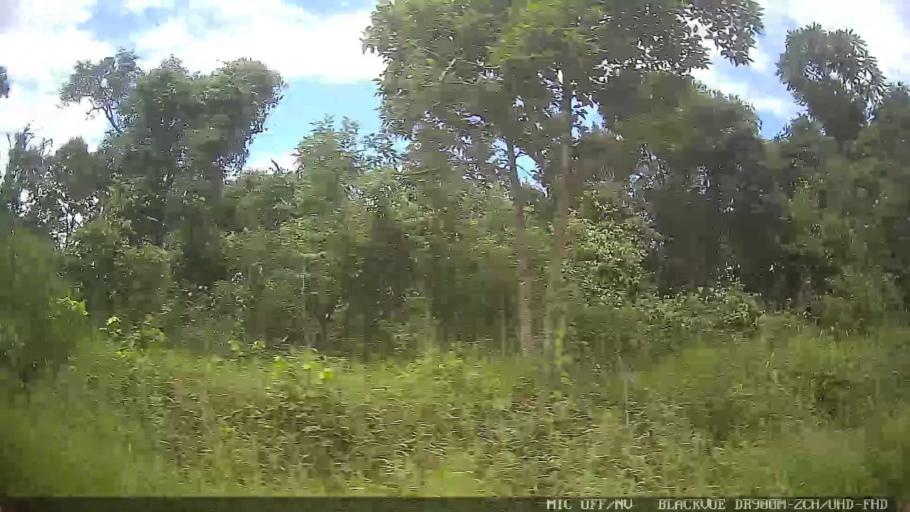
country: BR
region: Minas Gerais
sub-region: Extrema
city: Extrema
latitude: -22.7294
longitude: -46.4229
